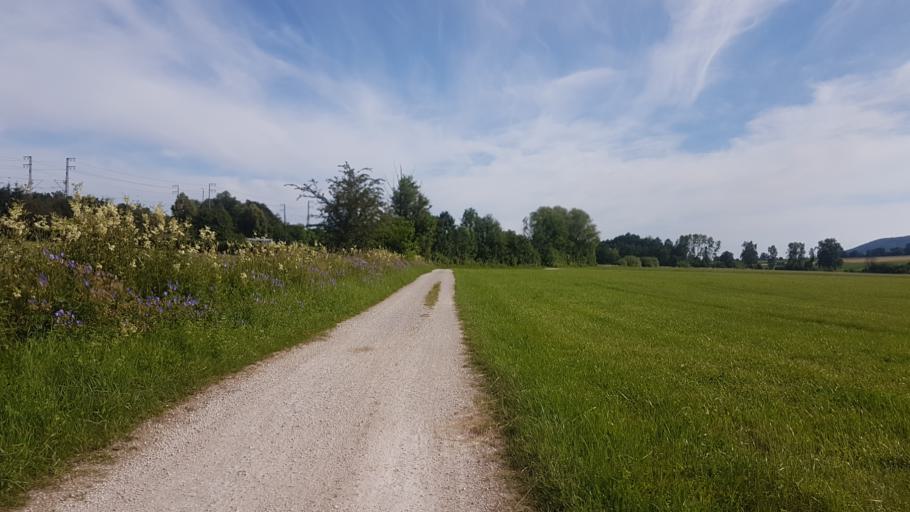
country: DE
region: Bavaria
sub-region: Regierungsbezirk Mittelfranken
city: Treuchtlingen
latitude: 48.9688
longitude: 10.9127
